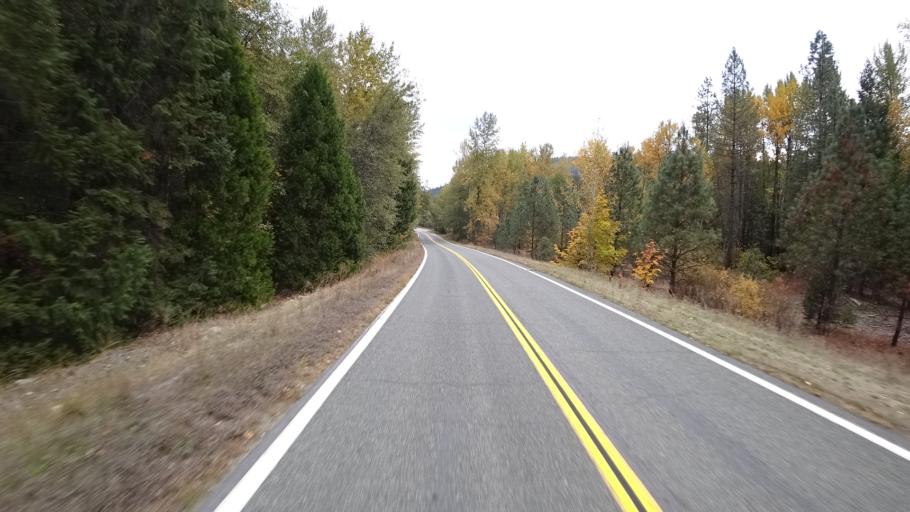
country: US
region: California
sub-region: Siskiyou County
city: Happy Camp
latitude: 41.9157
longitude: -123.4651
